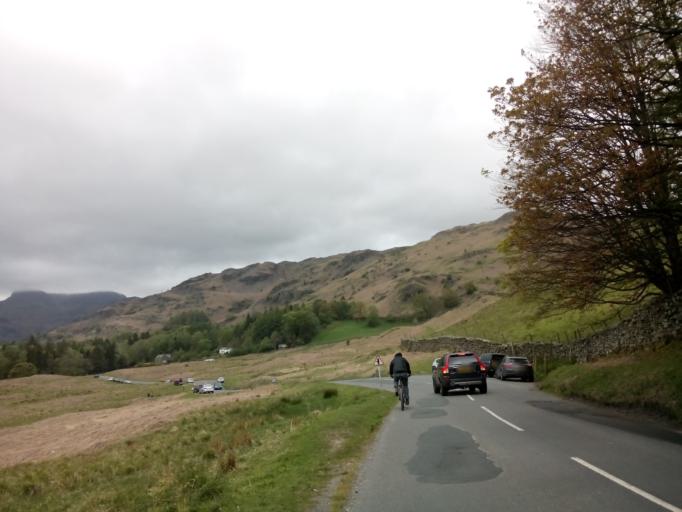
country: GB
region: England
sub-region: Cumbria
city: Ambleside
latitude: 54.4340
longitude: -3.0299
